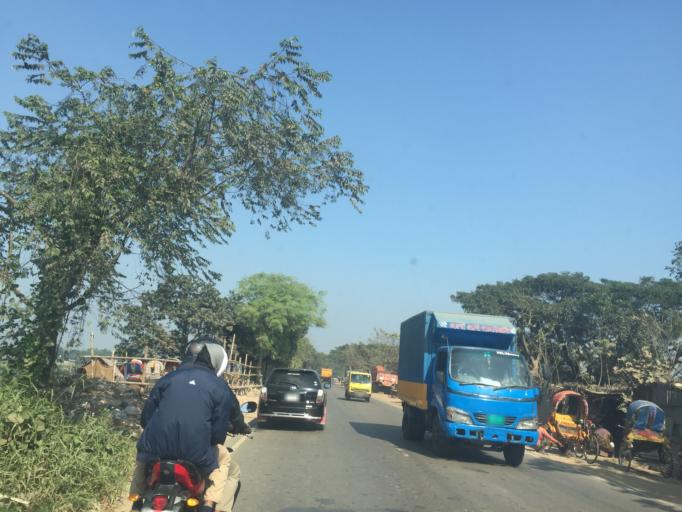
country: BD
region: Dhaka
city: Azimpur
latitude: 23.8129
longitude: 90.3403
